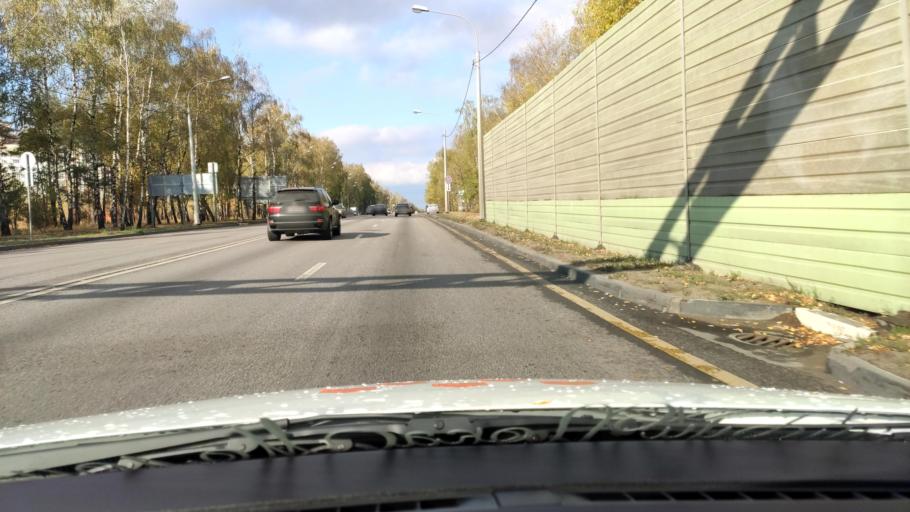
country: RU
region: Voronezj
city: Pridonskoy
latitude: 51.6856
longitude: 39.1144
